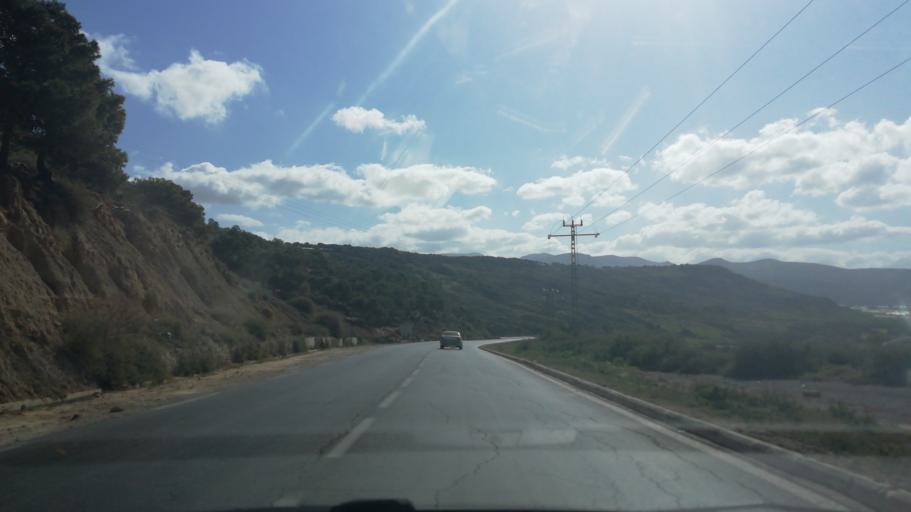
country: DZ
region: Relizane
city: Mazouna
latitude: 36.3090
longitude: 0.6675
